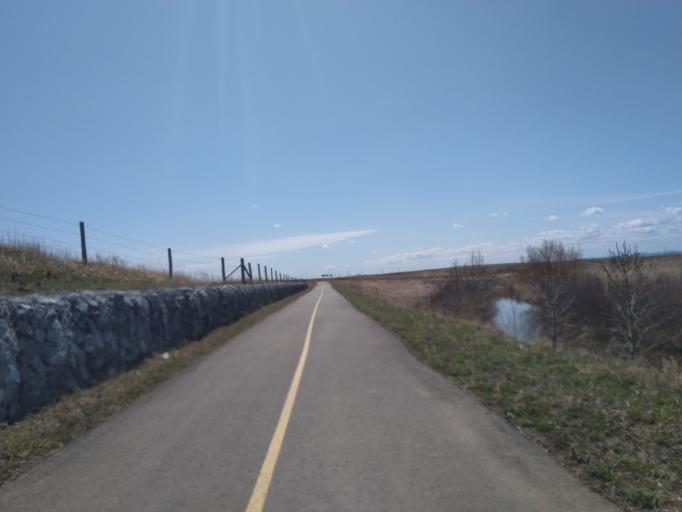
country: CA
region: Alberta
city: Chestermere
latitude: 51.0244
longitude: -113.9236
